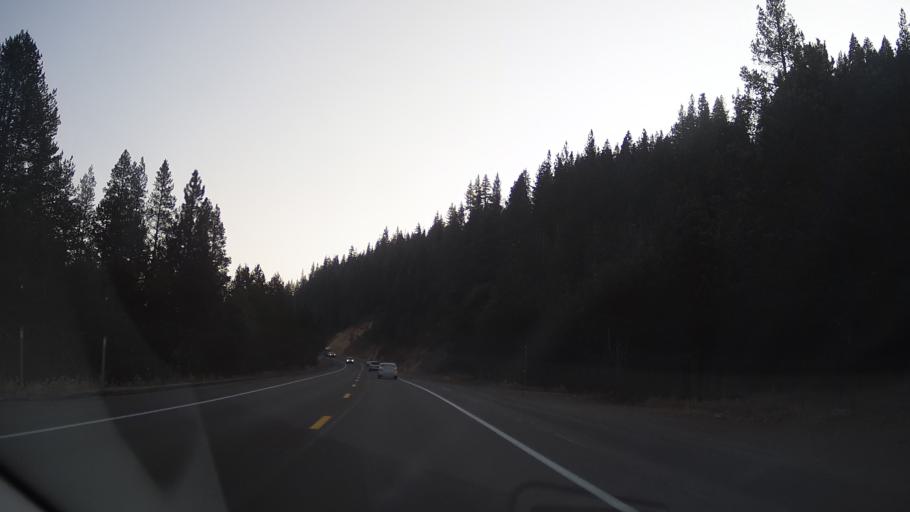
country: US
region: California
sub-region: Placer County
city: Sunnyside-Tahoe City
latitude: 39.2308
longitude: -120.2058
